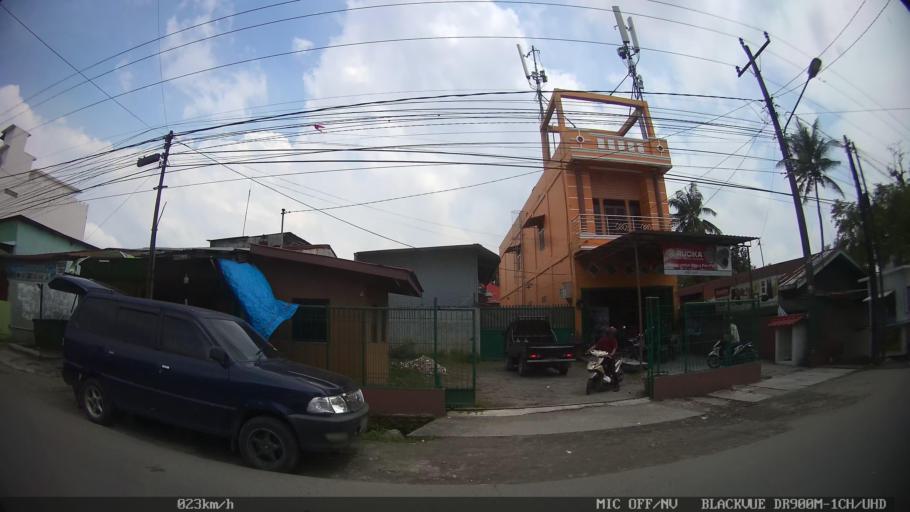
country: ID
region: North Sumatra
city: Labuhan Deli
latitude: 3.6570
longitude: 98.6740
